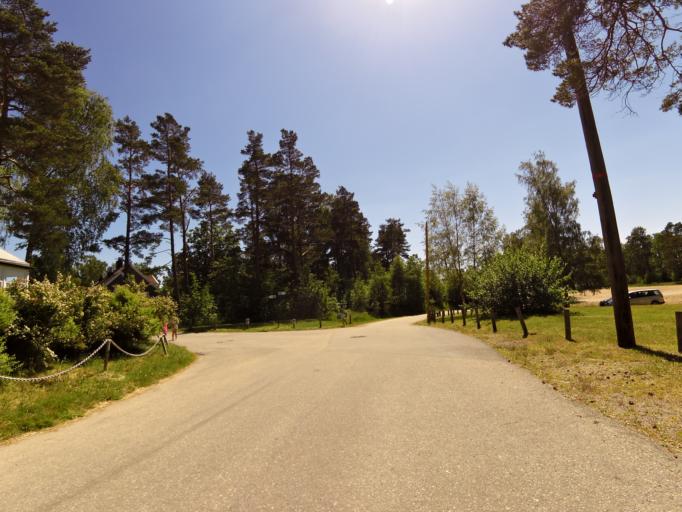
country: NO
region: Vest-Agder
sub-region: Kristiansand
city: Justvik
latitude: 58.1925
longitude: 8.0791
